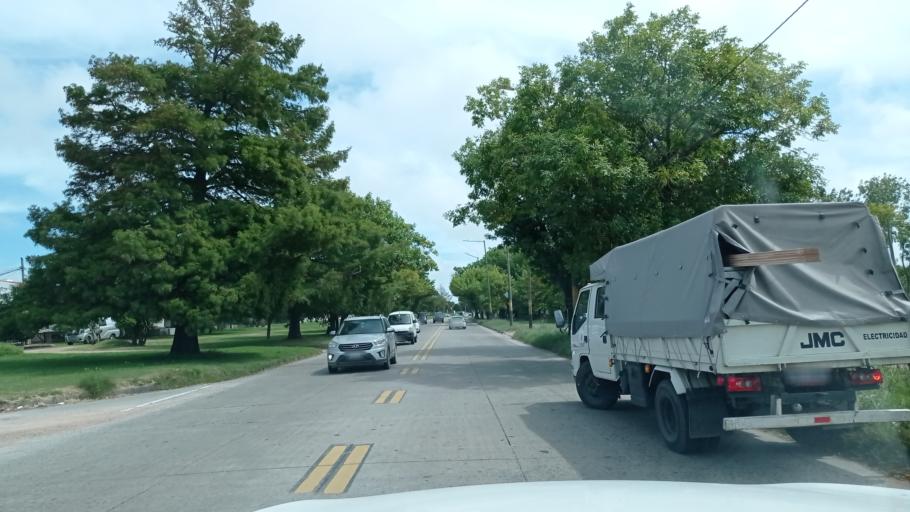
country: UY
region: Canelones
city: Paso de Carrasco
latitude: -34.8718
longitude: -56.0911
